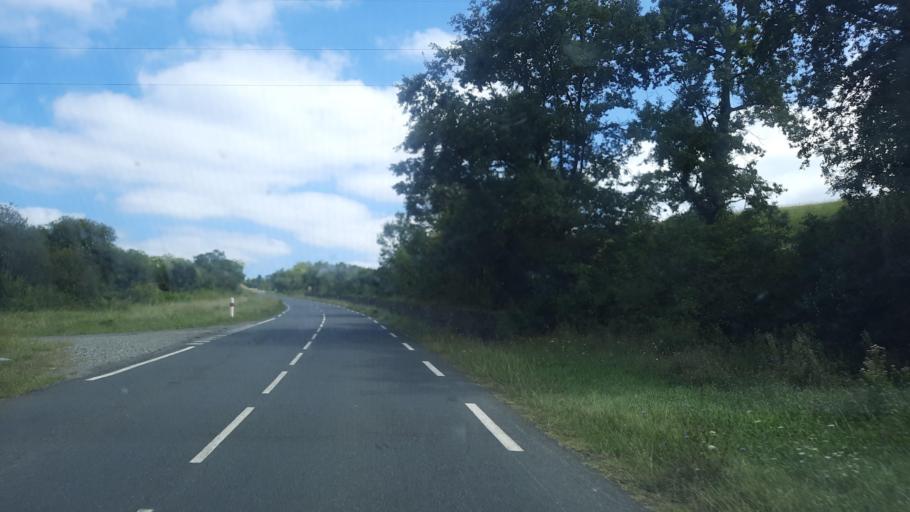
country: FR
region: Midi-Pyrenees
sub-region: Departement de la Haute-Garonne
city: Boulogne-sur-Gesse
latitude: 43.2911
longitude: 0.6324
